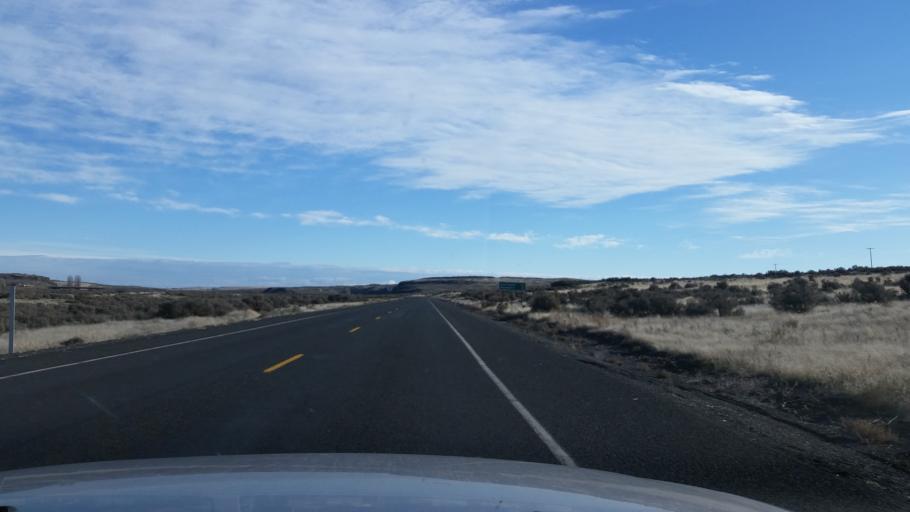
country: US
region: Washington
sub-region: Adams County
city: Ritzville
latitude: 47.3316
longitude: -118.6748
